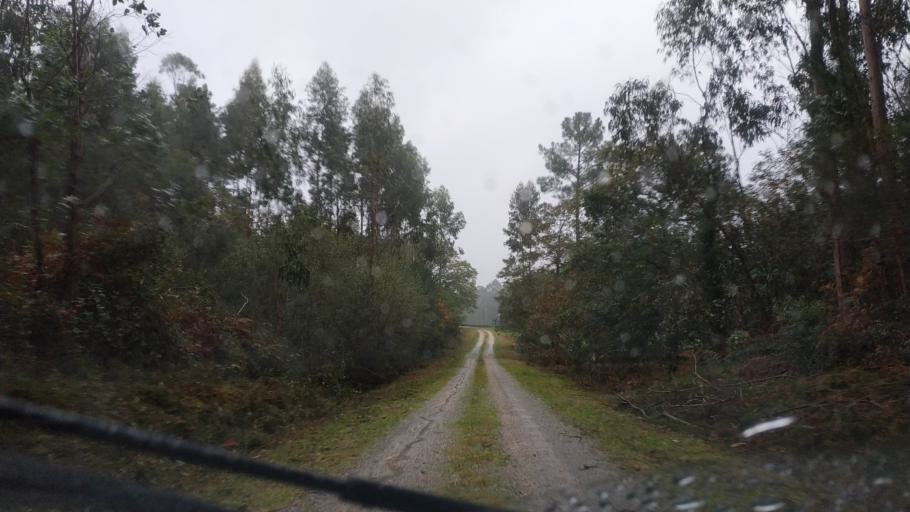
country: ES
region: Galicia
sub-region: Provincia da Coruna
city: Negreira
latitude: 42.9087
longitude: -8.7633
